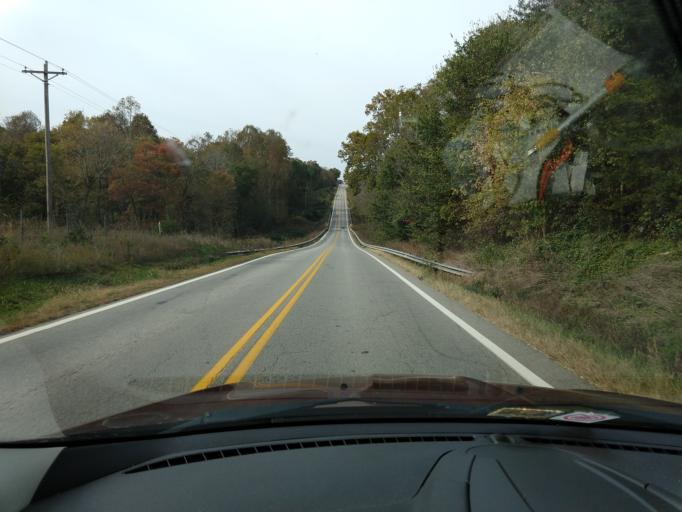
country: US
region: Virginia
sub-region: Pittsylvania County
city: Gretna
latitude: 36.9447
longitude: -79.4874
